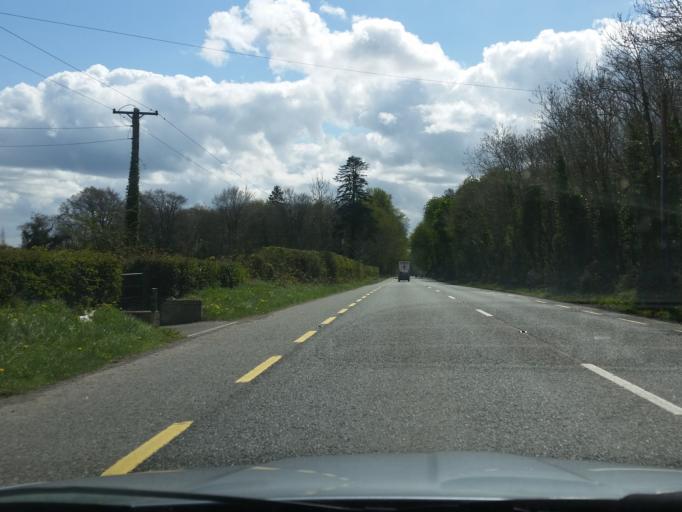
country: IE
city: Kentstown
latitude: 53.6302
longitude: -6.4918
